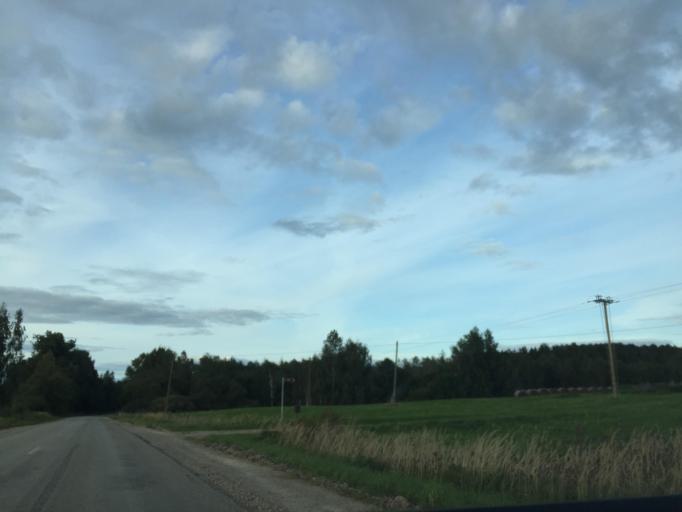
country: LV
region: Nereta
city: Nereta
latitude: 56.2914
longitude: 25.4142
